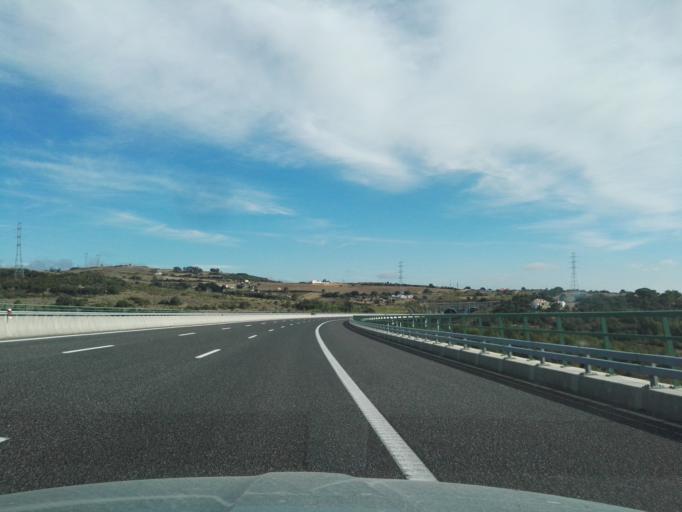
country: PT
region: Lisbon
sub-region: Arruda Dos Vinhos
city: Arruda dos Vinhos
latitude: 38.9351
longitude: -9.0733
